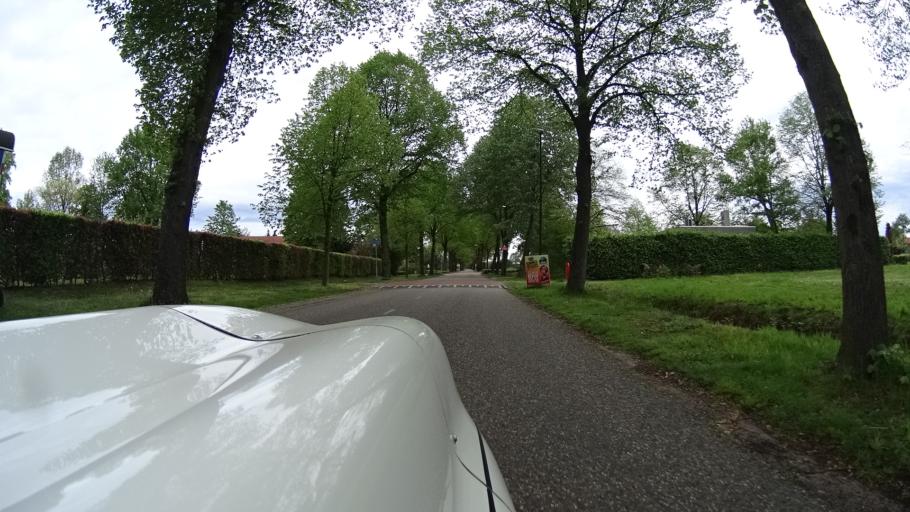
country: NL
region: North Brabant
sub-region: Gemeente Boekel
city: Boekel
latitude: 51.5404
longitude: 5.7094
